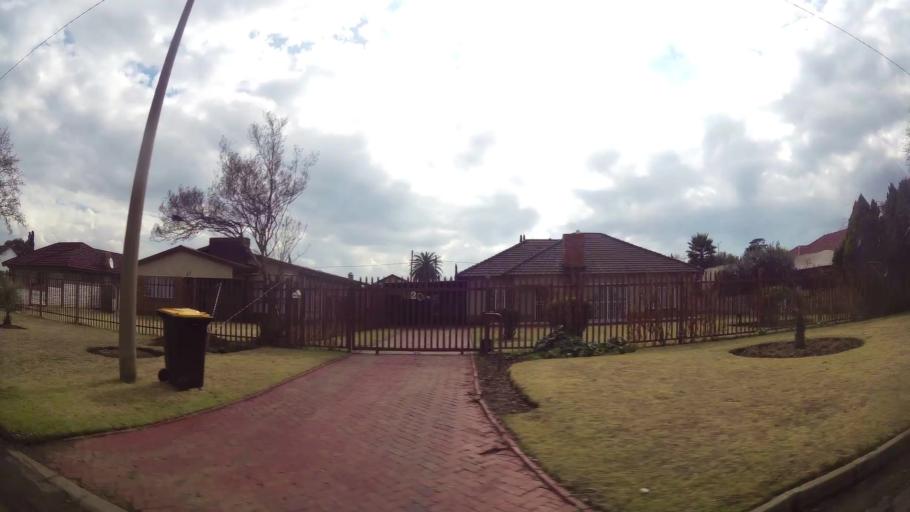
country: ZA
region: Gauteng
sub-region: Sedibeng District Municipality
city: Vereeniging
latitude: -26.6544
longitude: 27.9837
